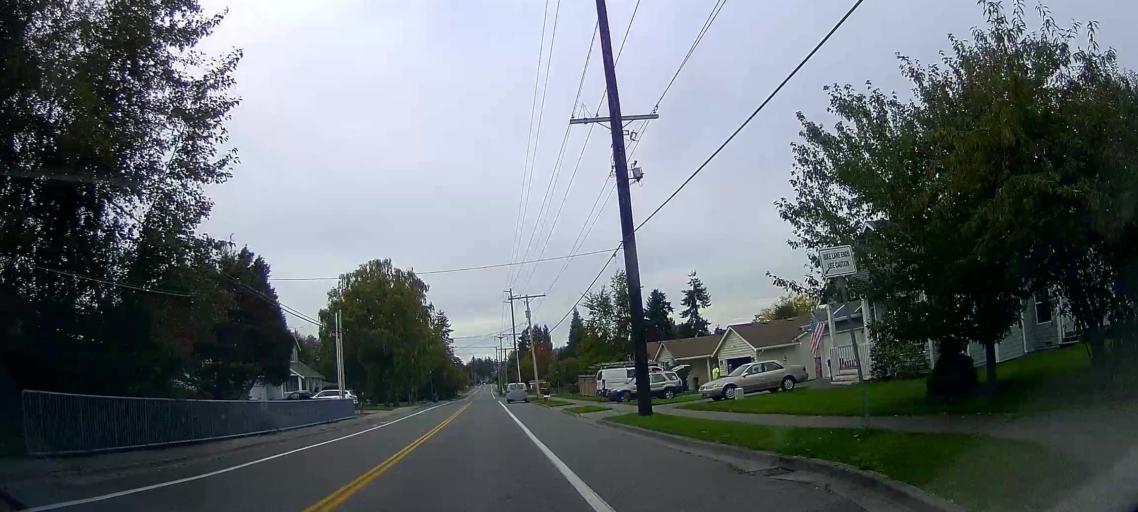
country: US
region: Washington
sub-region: Skagit County
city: Anacortes
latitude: 48.4889
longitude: -122.6252
